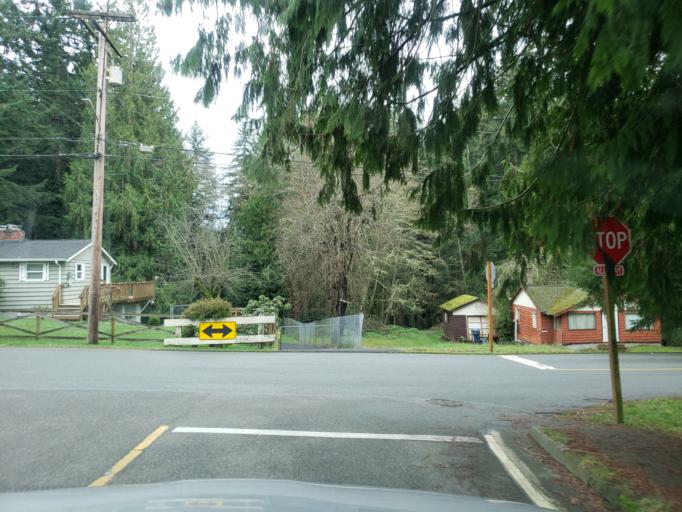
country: US
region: Washington
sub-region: Snohomish County
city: Esperance
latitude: 47.8123
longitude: -122.3439
